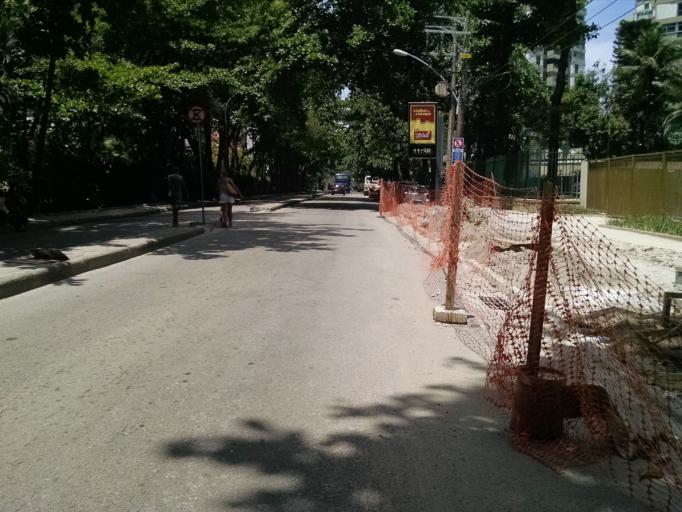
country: BR
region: Rio de Janeiro
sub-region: Rio De Janeiro
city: Rio de Janeiro
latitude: -22.9943
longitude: -43.2542
